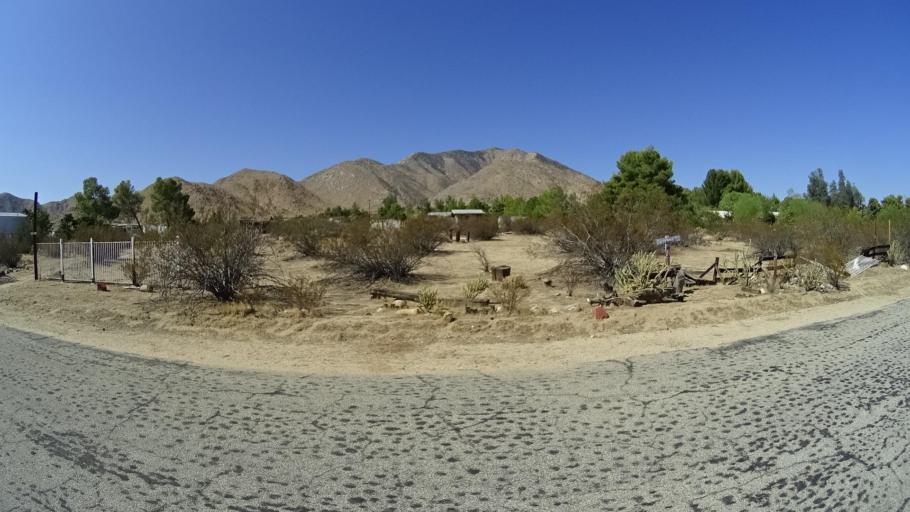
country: US
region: California
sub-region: San Diego County
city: Julian
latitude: 33.0707
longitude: -116.4347
